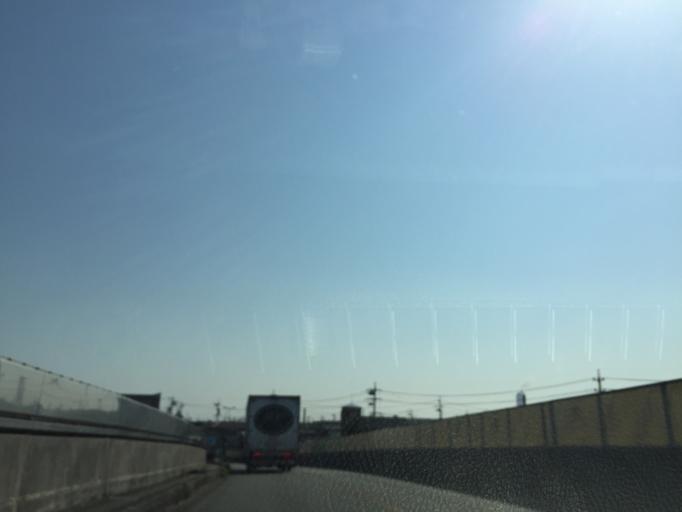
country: JP
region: Mie
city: Yokkaichi
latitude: 35.0007
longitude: 136.6524
